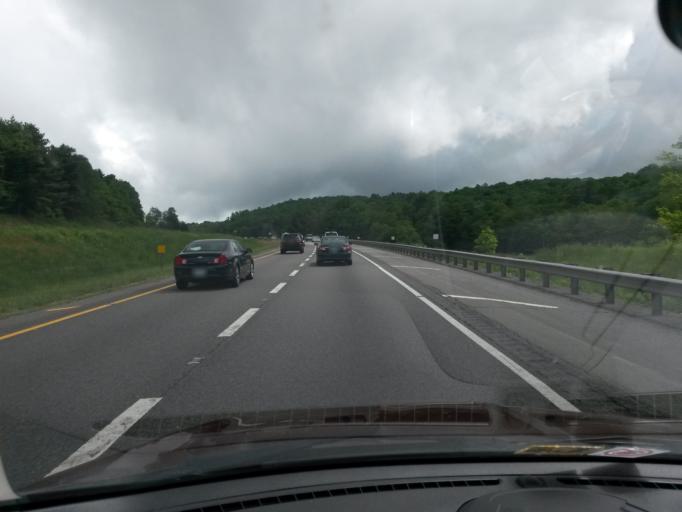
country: US
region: Virginia
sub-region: Carroll County
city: Cana
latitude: 36.6643
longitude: -80.7097
